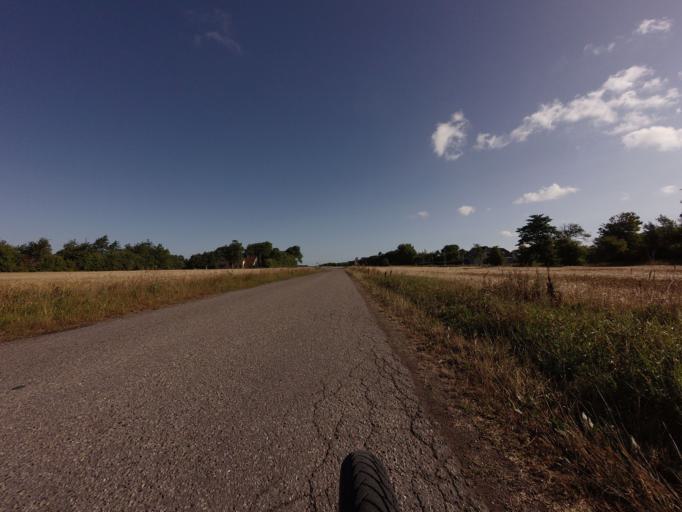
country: DK
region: North Denmark
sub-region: Hjorring Kommune
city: Vra
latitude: 57.3937
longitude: 9.9529
